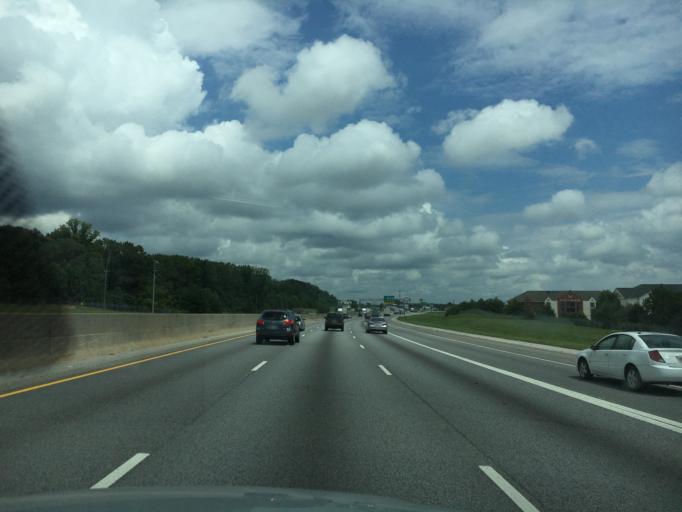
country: US
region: Georgia
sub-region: DeKalb County
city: Lithonia
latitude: 33.7024
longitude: -84.1024
